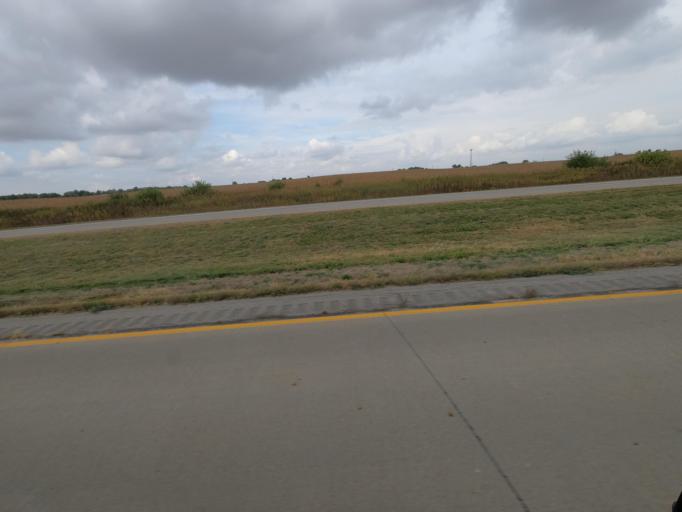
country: US
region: Iowa
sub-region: Jasper County
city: Prairie City
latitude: 41.5880
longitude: -93.2218
